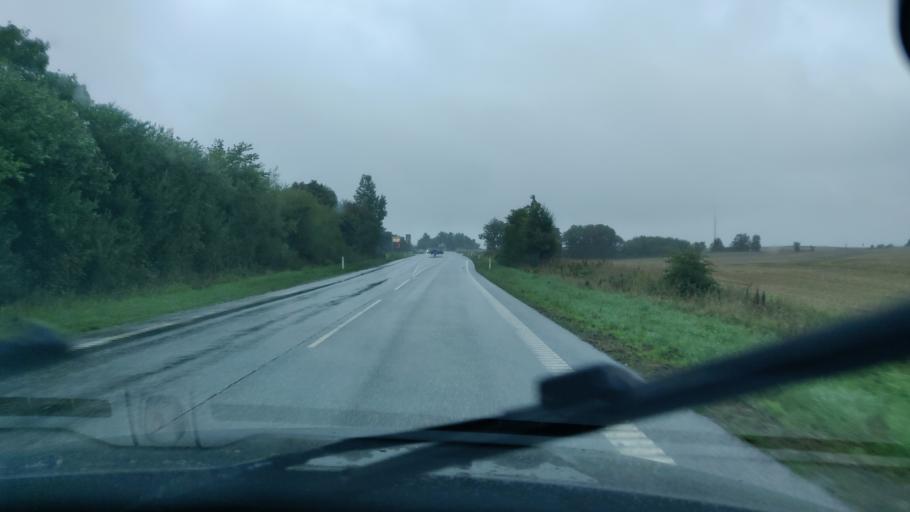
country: DK
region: North Denmark
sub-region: Thisted Kommune
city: Hurup
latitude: 56.8441
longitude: 8.5289
